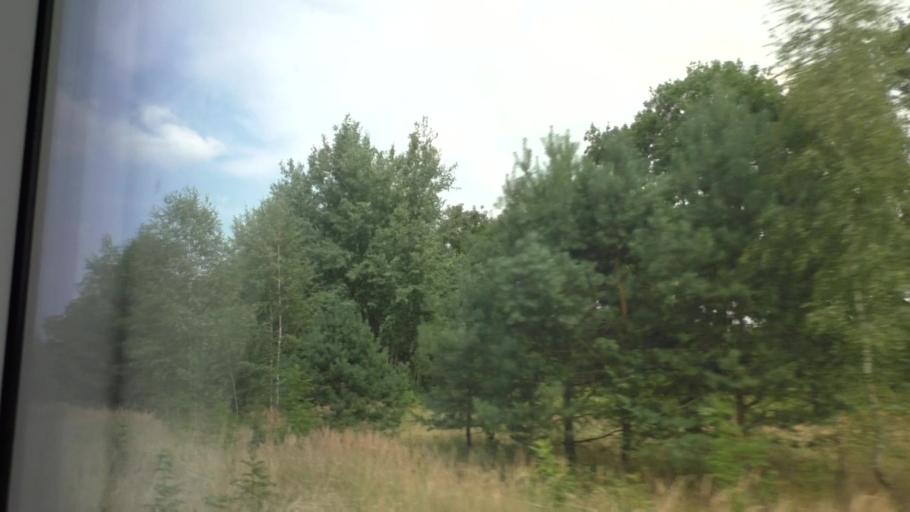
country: DE
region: Brandenburg
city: Mixdorf
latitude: 52.1676
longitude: 14.3795
